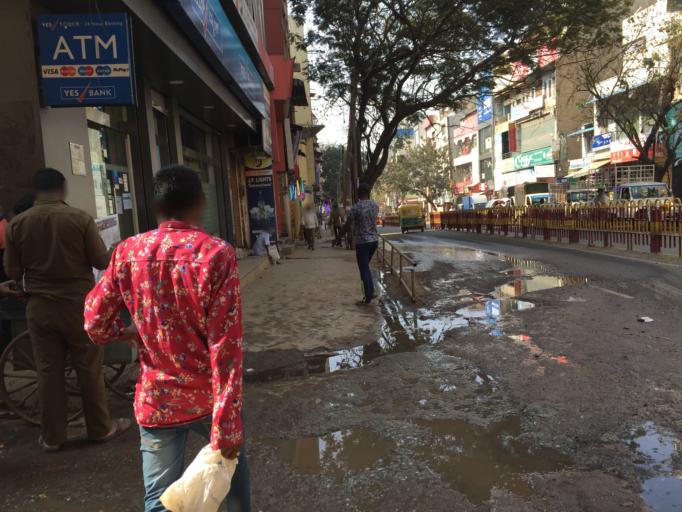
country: IN
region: Karnataka
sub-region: Bangalore Urban
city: Bangalore
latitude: 12.9728
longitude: 77.5772
